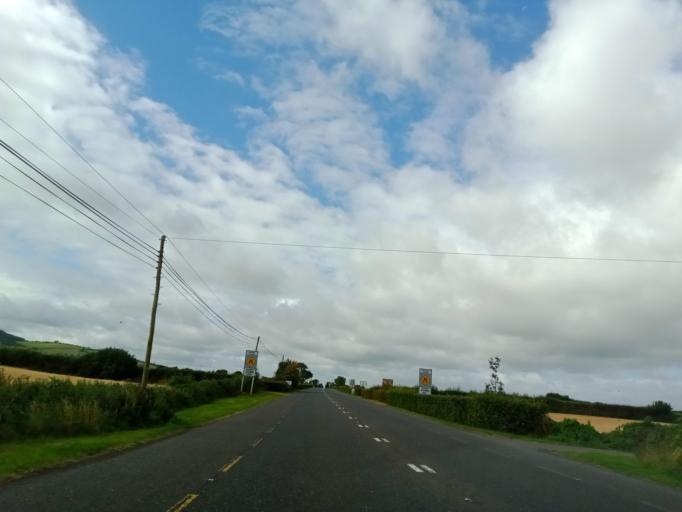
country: IE
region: Leinster
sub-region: Laois
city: Rathdowney
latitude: 52.8235
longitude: -7.4671
